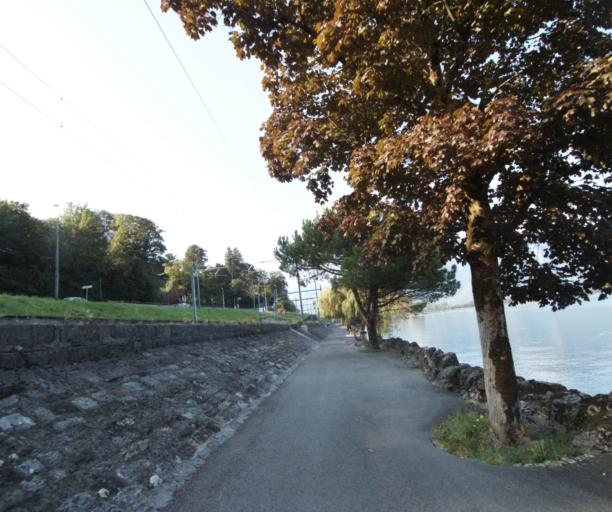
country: CH
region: Vaud
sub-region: Aigle District
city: Villeneuve
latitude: 46.4066
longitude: 6.9303
